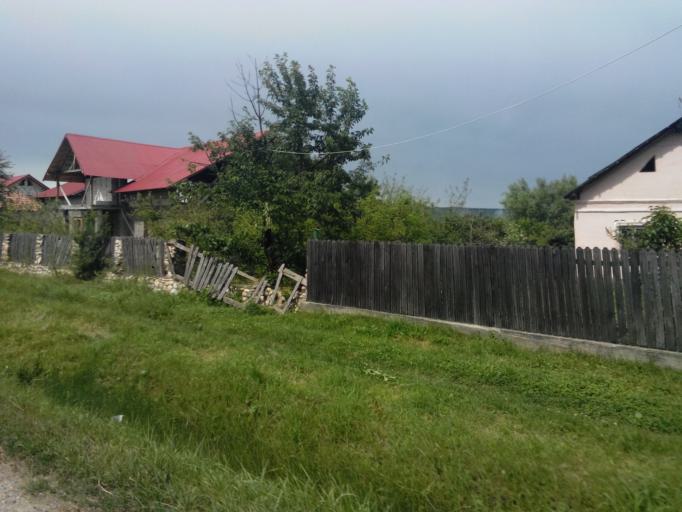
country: RO
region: Arges
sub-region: Comuna Budeasa
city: Galasesti
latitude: 44.9338
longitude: 24.7787
